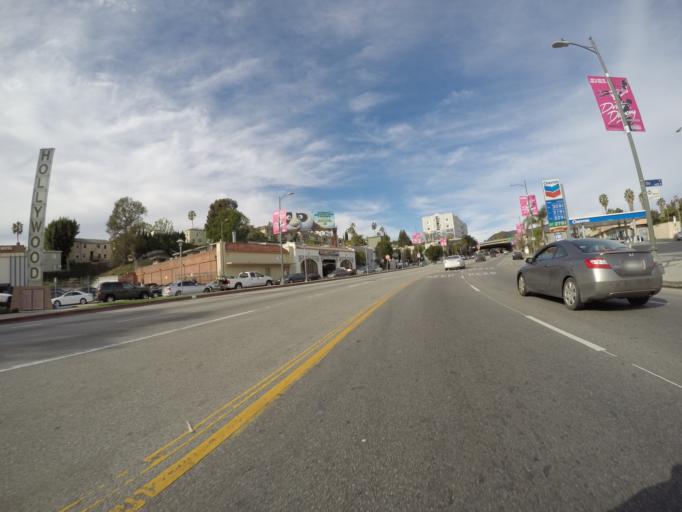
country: US
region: California
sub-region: Los Angeles County
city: Hollywood
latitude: 34.1055
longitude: -118.3305
